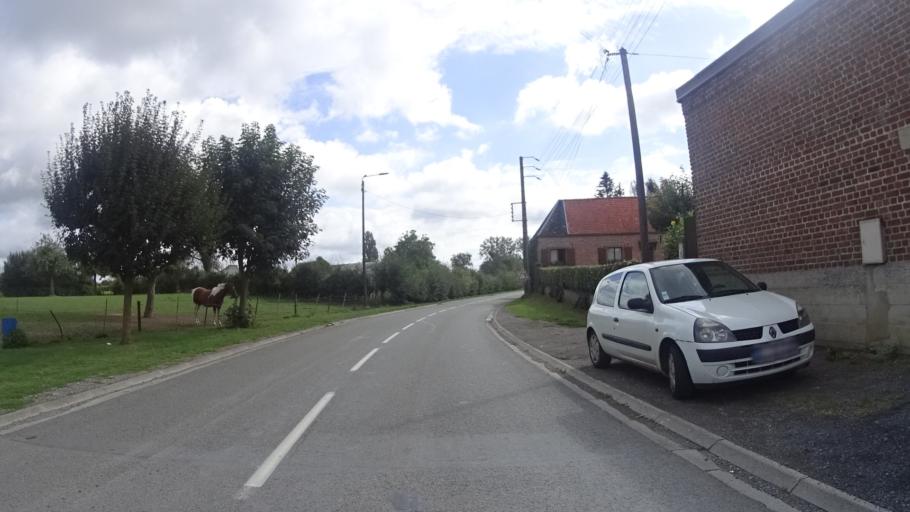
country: FR
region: Nord-Pas-de-Calais
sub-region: Departement du Nord
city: Bousies
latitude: 50.0984
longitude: 3.6398
